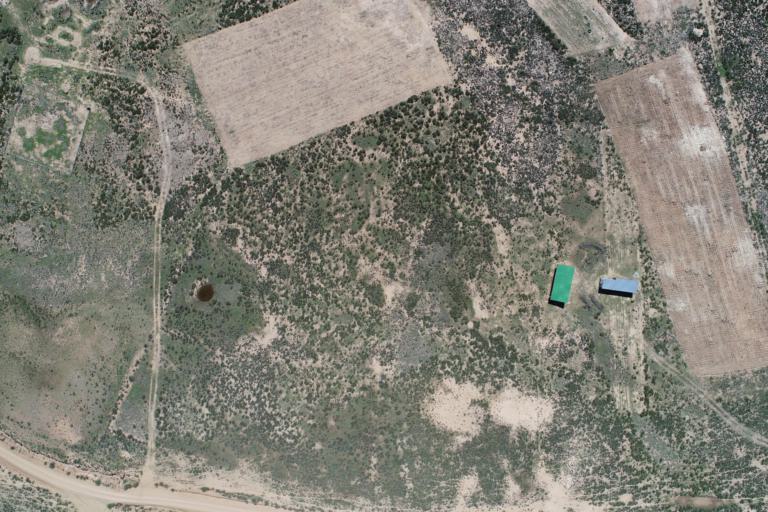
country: BO
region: La Paz
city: Patacamaya
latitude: -17.2937
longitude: -68.4871
